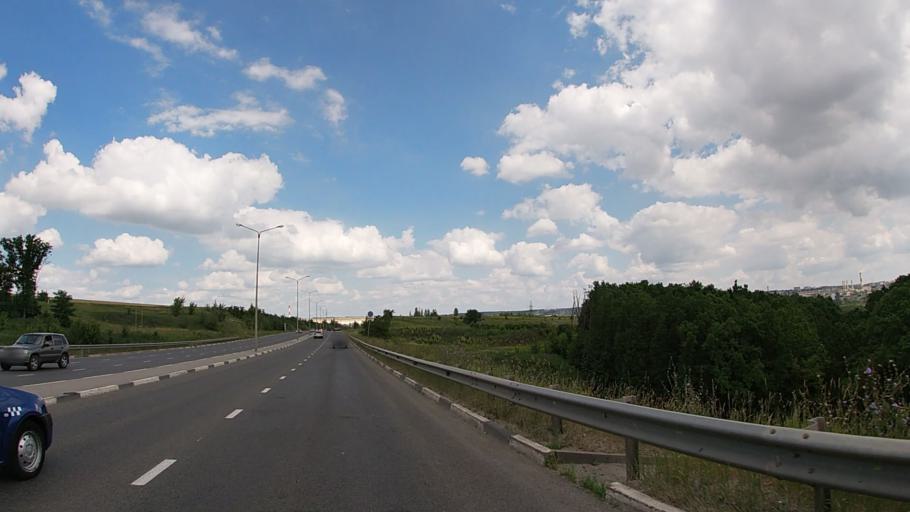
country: RU
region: Belgorod
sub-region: Belgorodskiy Rayon
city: Belgorod
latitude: 50.6000
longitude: 36.5302
